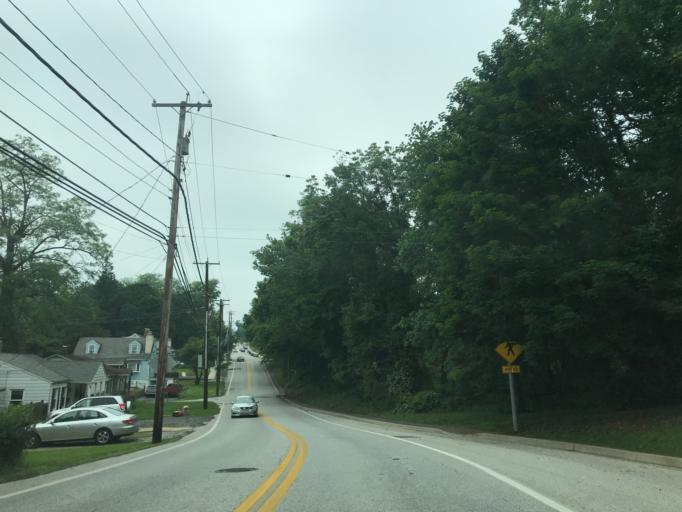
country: US
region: Maryland
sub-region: Baltimore County
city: Charlestown
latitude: 39.2712
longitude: -76.7094
